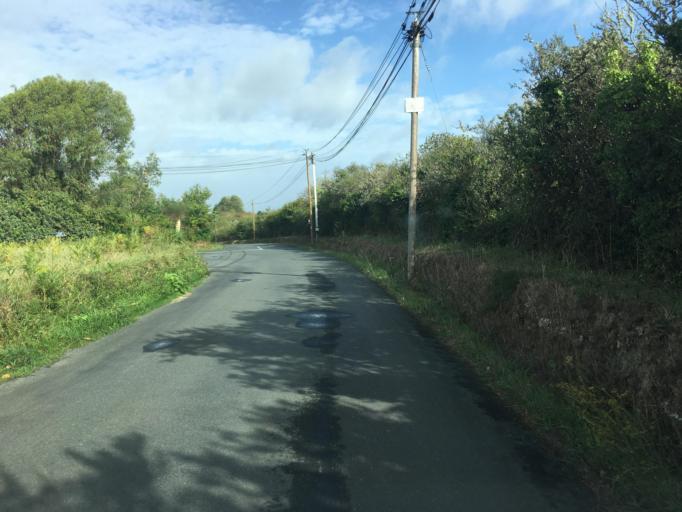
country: FR
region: Brittany
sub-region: Departement du Finistere
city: Plobannalec-Lesconil
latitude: 47.8136
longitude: -4.1885
